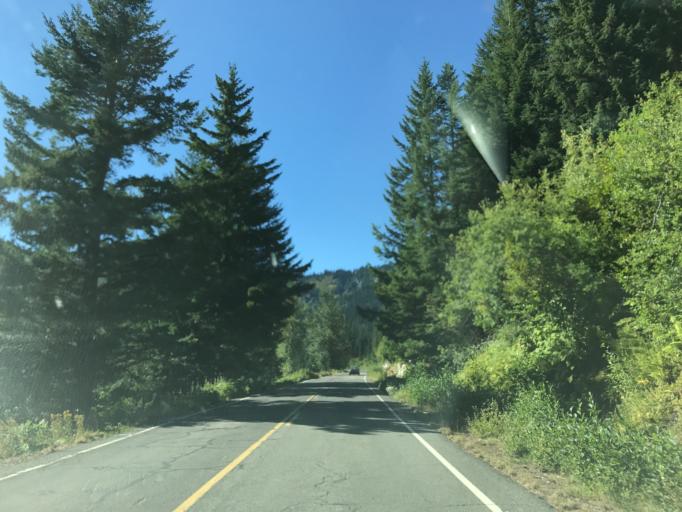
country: US
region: Washington
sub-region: Pierce County
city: Buckley
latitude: 46.7722
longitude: -121.6932
